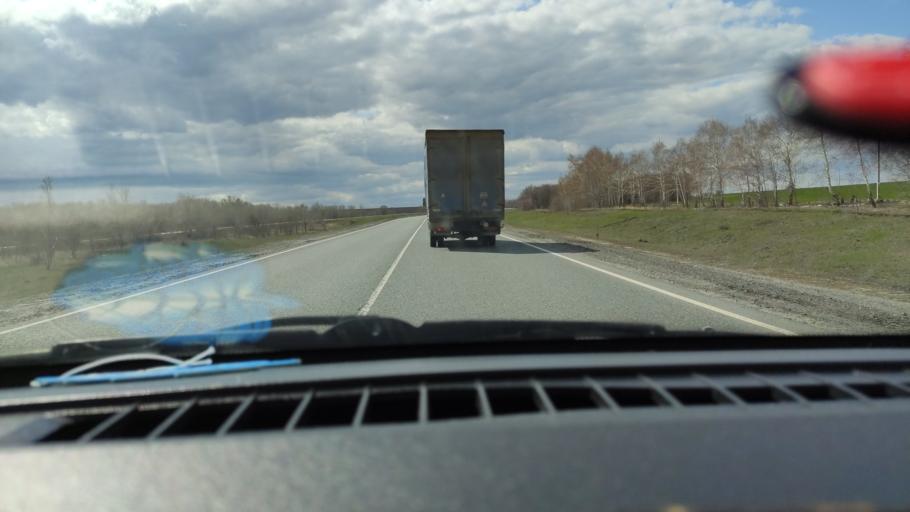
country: RU
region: Saratov
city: Balakovo
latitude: 52.1079
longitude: 47.7454
